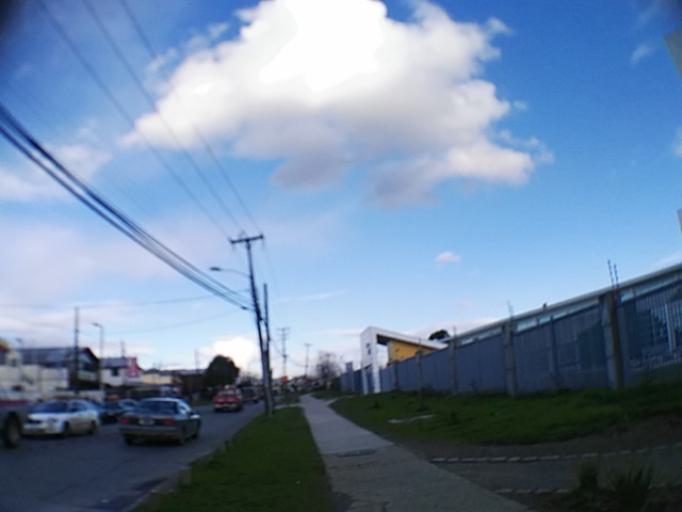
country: CL
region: Los Lagos
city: Las Animas
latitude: -39.8365
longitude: -73.2199
